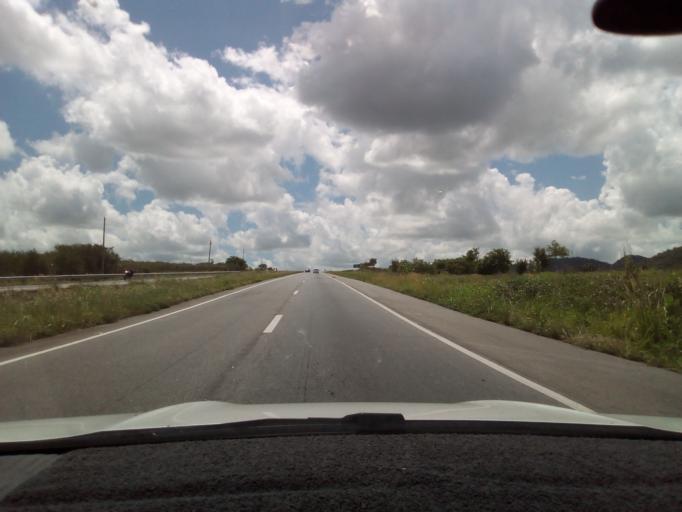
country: BR
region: Paraiba
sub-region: Gurinhem
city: Gurinhem
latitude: -7.1839
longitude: -35.4417
